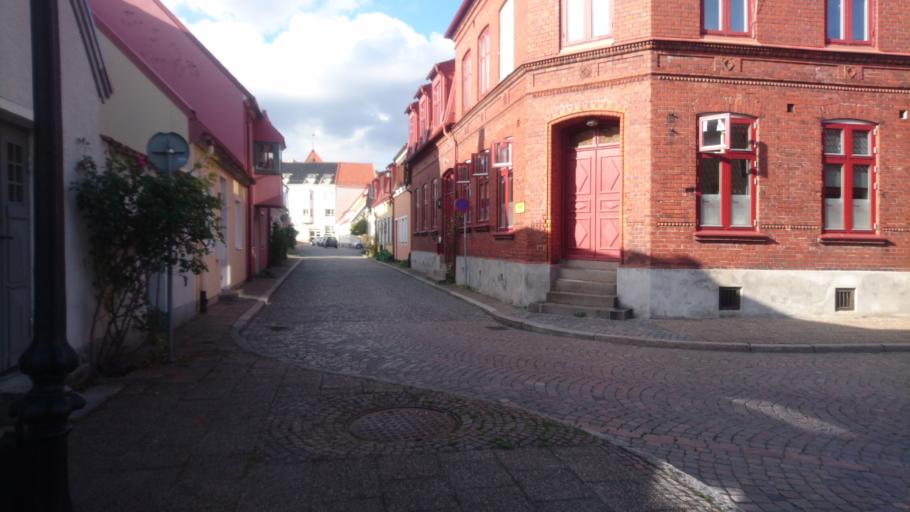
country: SE
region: Skane
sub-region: Ystads Kommun
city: Ystad
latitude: 55.4287
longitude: 13.8232
